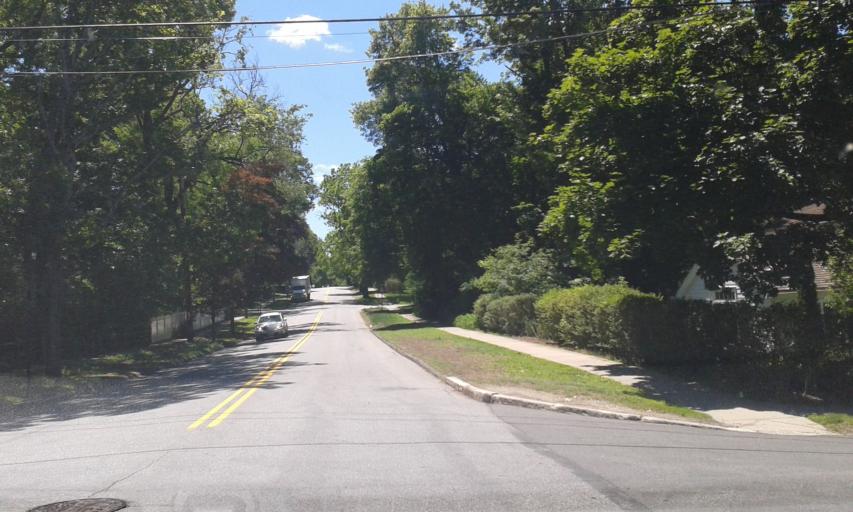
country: US
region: Massachusetts
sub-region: Middlesex County
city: Winchester
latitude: 42.4643
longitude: -71.1222
